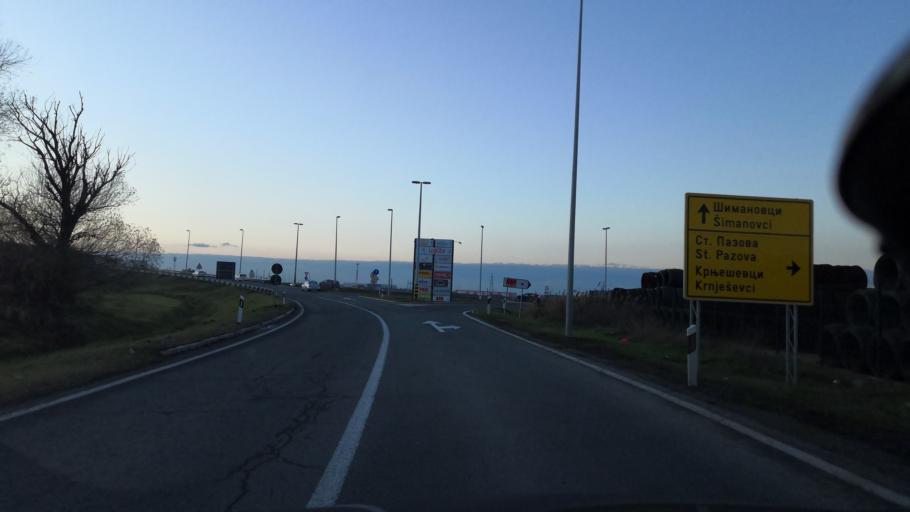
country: RS
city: Simanovci
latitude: 44.8773
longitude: 20.1287
